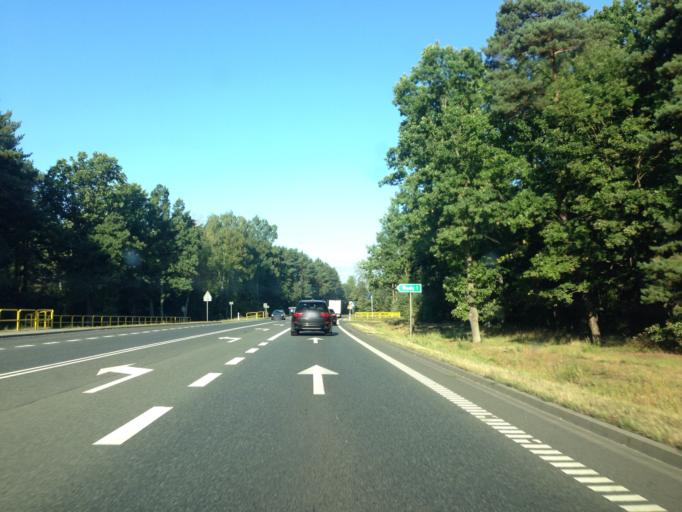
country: PL
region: Kujawsko-Pomorskie
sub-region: Powiat bydgoski
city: Solec Kujawski
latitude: 53.0611
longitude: 18.1859
